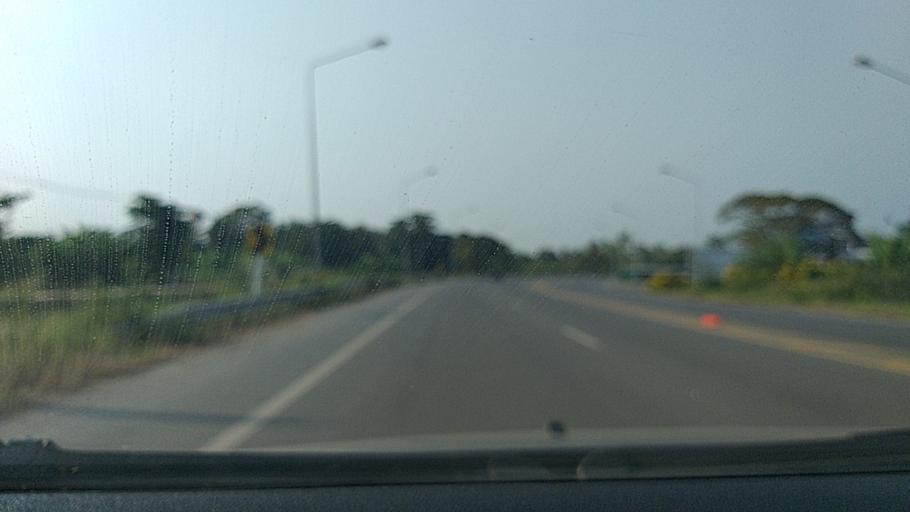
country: TH
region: Sing Buri
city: Sing Buri
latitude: 14.8610
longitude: 100.4064
